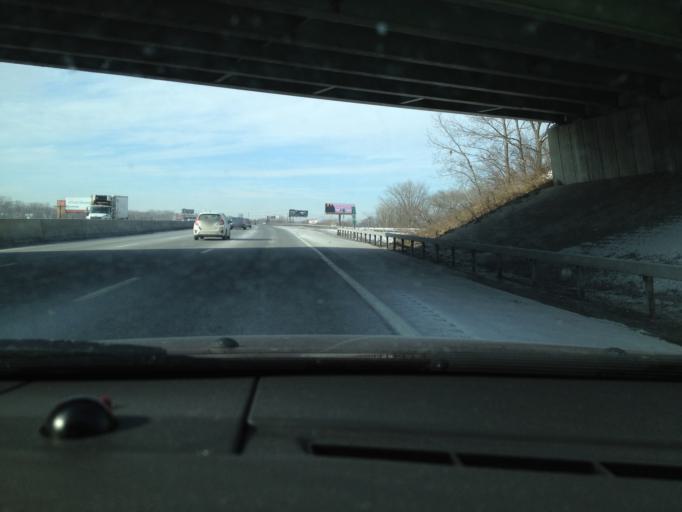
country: US
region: New York
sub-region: Albany County
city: West Albany
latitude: 42.6810
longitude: -73.7727
